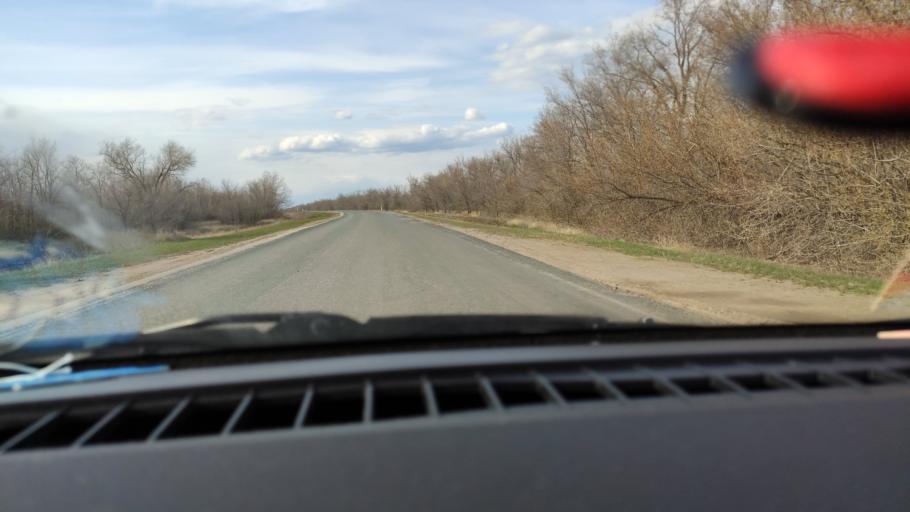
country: RU
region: Saratov
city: Rovnoye
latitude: 50.9820
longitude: 46.1149
